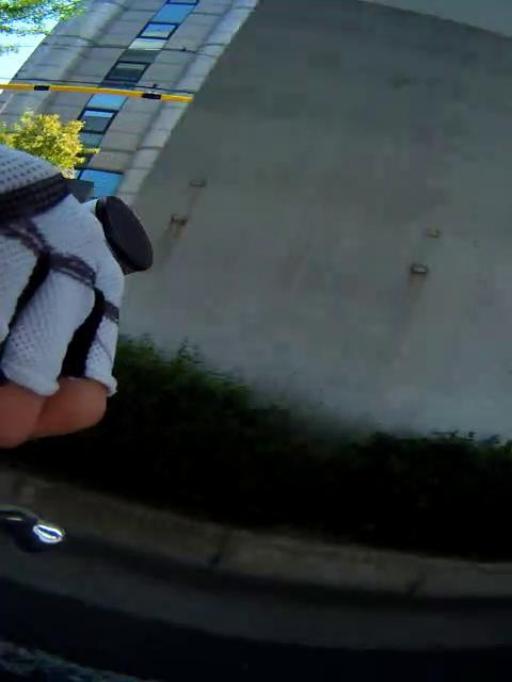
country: JP
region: Osaka
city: Matsubara
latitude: 34.5943
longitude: 135.5502
